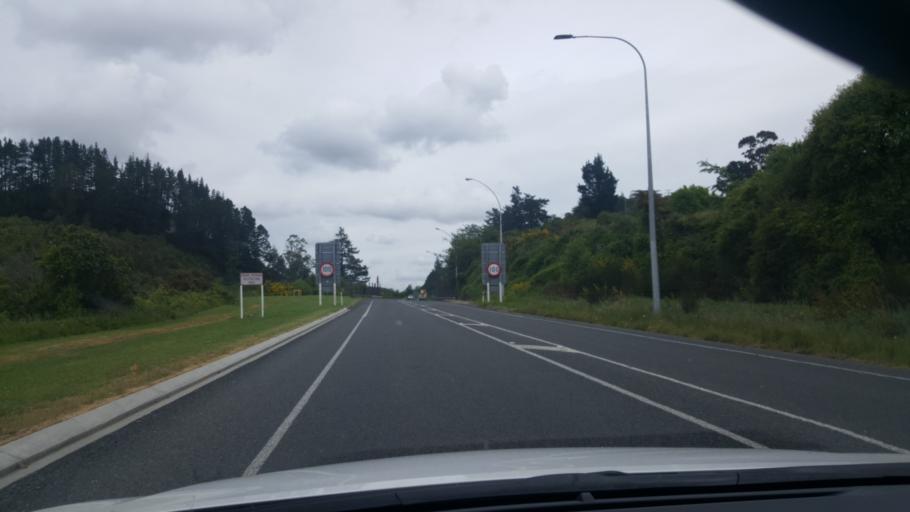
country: NZ
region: Bay of Plenty
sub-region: Rotorua District
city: Rotorua
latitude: -38.1680
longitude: 176.2455
